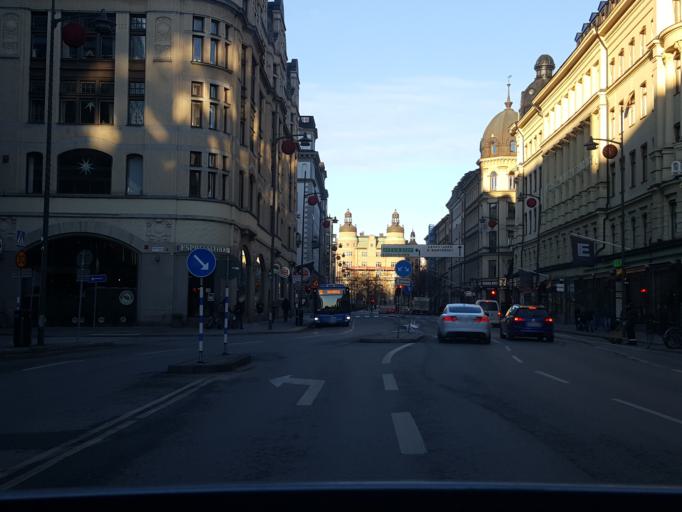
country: SE
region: Stockholm
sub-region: Stockholms Kommun
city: Stockholm
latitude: 59.3329
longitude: 18.0571
